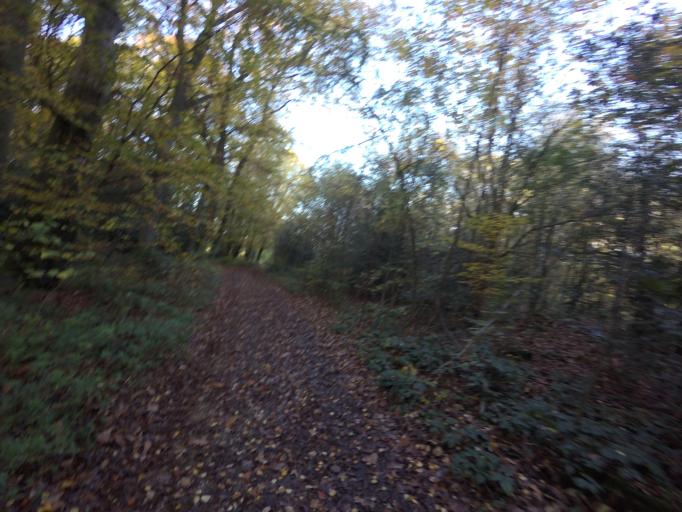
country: BE
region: Wallonia
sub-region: Province de Liege
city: Plombieres
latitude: 50.7824
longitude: 5.9397
